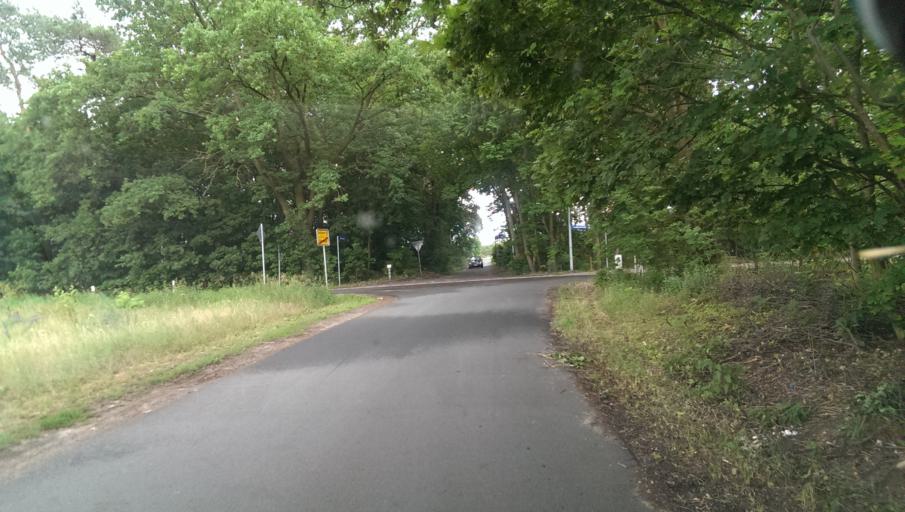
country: DE
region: Brandenburg
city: Stahnsdorf
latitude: 52.3662
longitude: 13.2127
